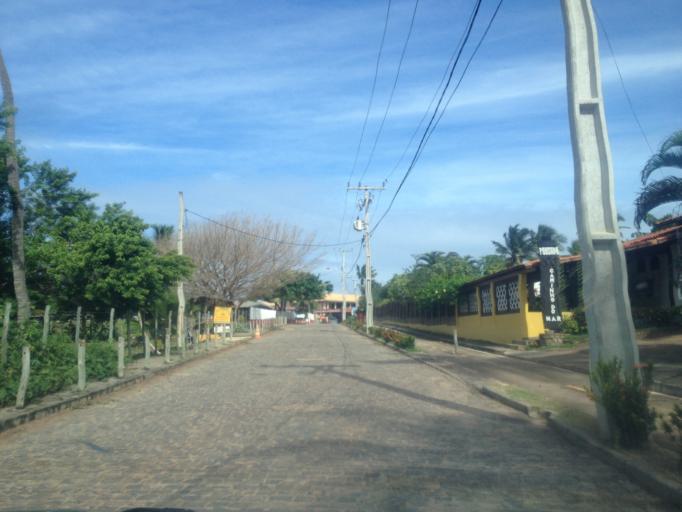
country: BR
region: Bahia
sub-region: Mata De Sao Joao
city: Mata de Sao Joao
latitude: -12.4996
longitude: -37.9632
